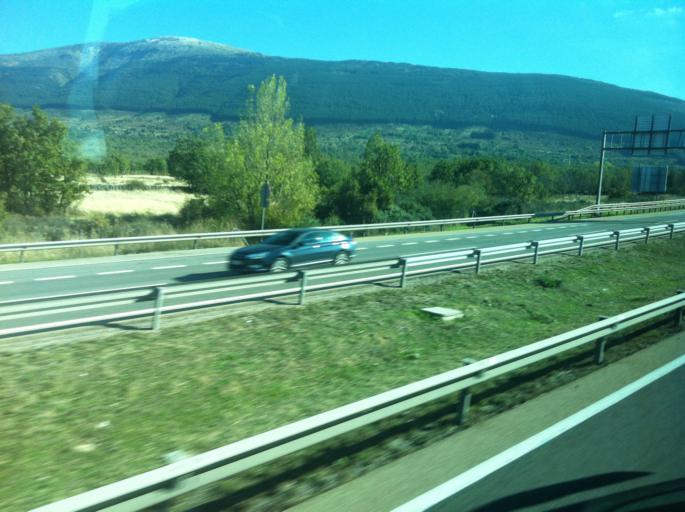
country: ES
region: Castille and Leon
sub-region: Provincia de Segovia
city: Cerezo de Abajo
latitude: 41.1852
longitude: -3.5851
